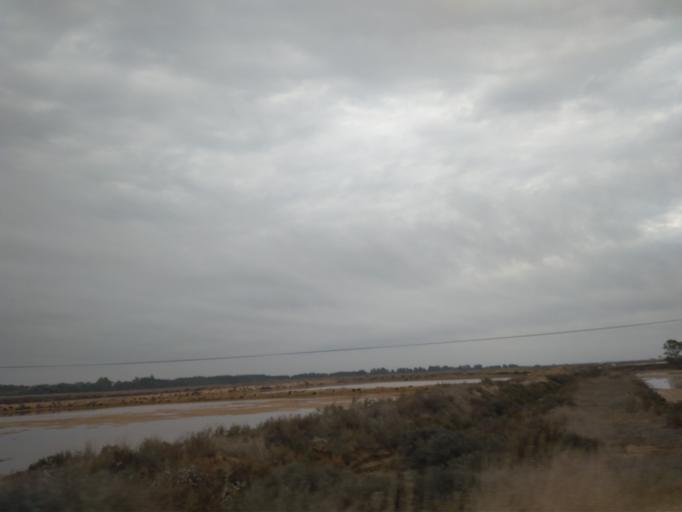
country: PT
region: Faro
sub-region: Faro
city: Faro
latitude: 37.0326
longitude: -7.9925
